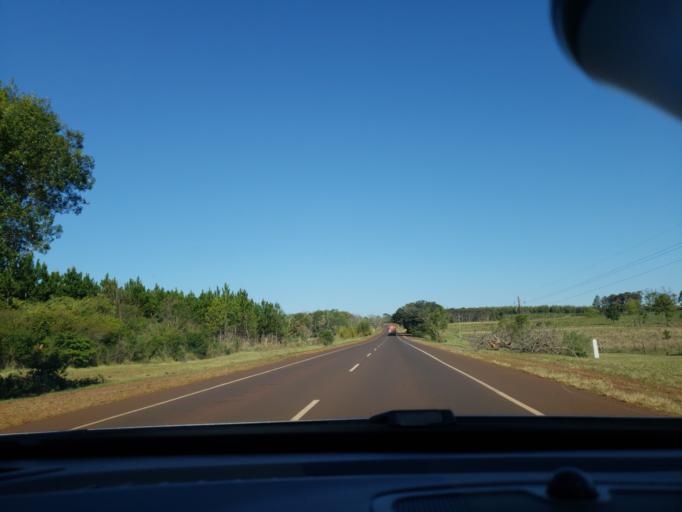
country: AR
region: Misiones
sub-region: Departamento de Apostoles
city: San Jose
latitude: -27.7920
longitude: -55.7715
